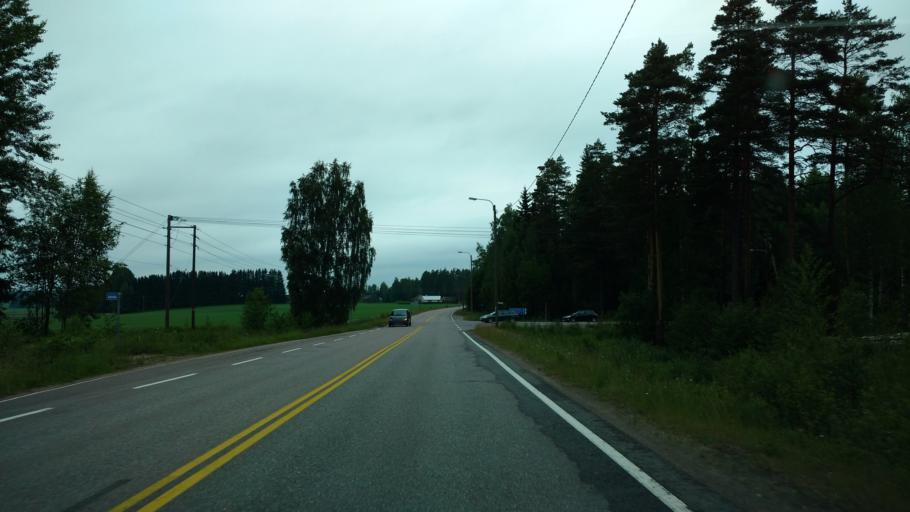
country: FI
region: Varsinais-Suomi
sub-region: Salo
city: Kiikala
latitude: 60.4283
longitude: 23.5921
